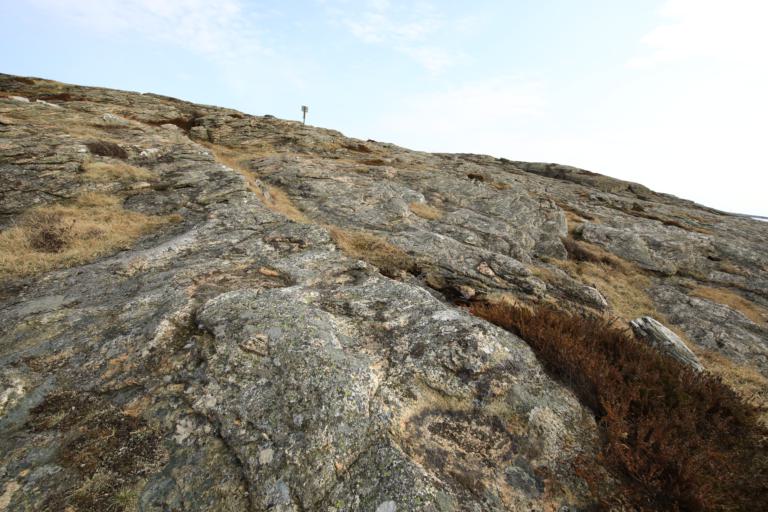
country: SE
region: Halland
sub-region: Kungsbacka Kommun
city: Frillesas
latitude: 57.2535
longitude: 12.0905
